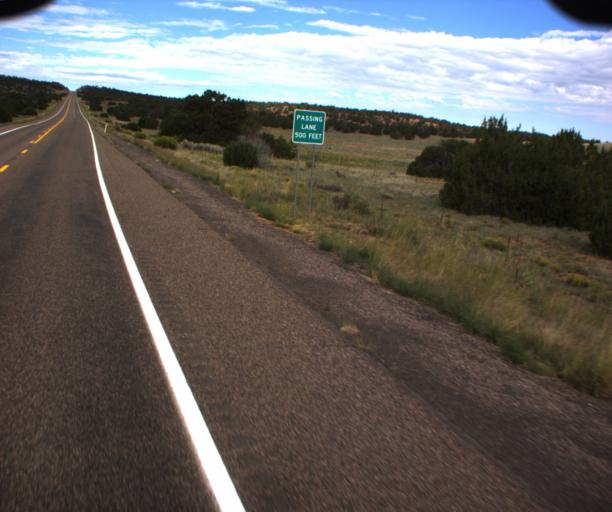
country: US
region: Arizona
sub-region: Apache County
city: Springerville
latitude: 34.1522
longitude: -109.1570
